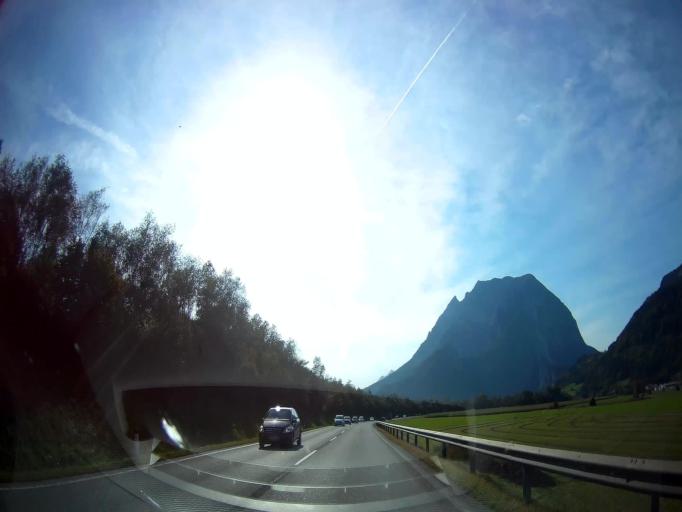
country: AT
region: Styria
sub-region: Politischer Bezirk Liezen
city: Stainach
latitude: 47.5259
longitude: 14.1091
